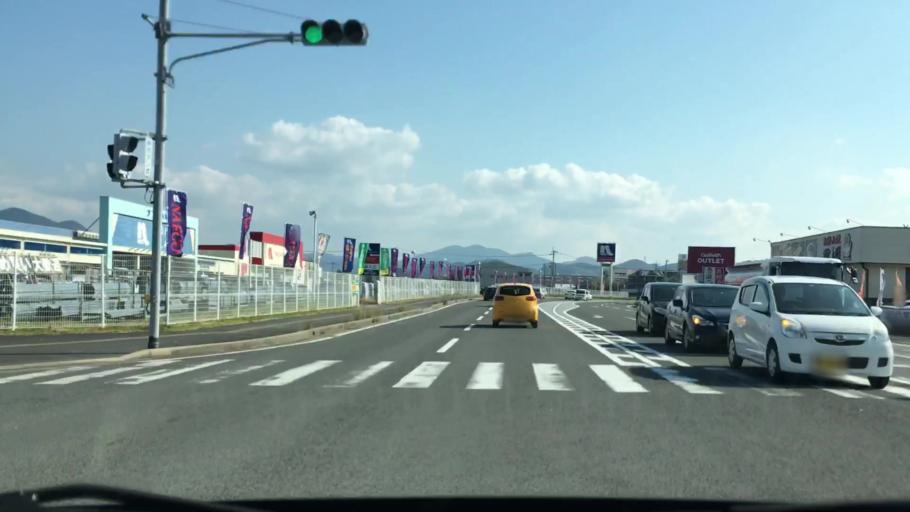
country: JP
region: Nagasaki
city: Togitsu
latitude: 32.8499
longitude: 129.8287
